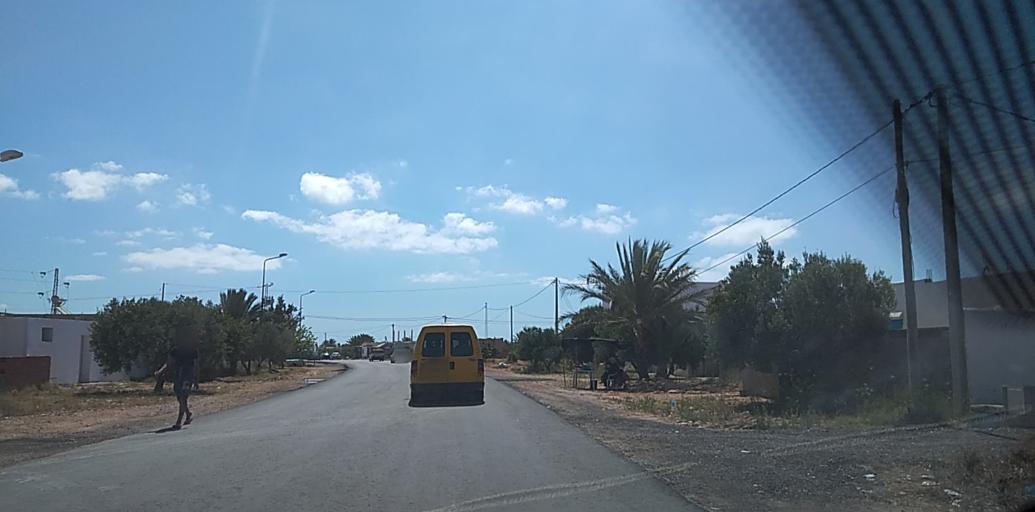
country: TN
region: Safaqis
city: Al Qarmadah
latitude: 34.6563
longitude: 11.0902
